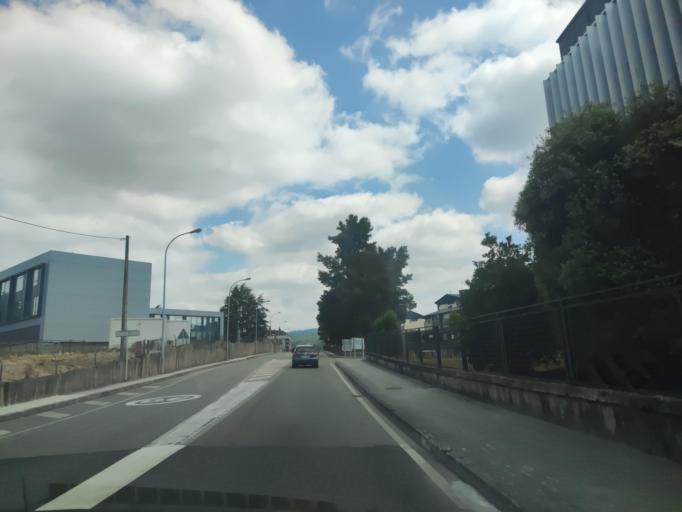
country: ES
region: Galicia
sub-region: Provincia de Pontevedra
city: Porrino
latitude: 42.1545
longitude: -8.6317
